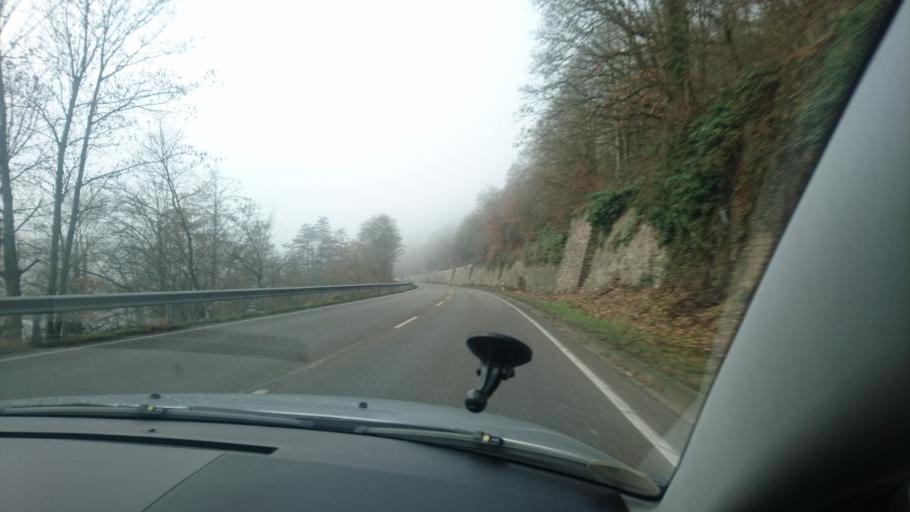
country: DE
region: Rheinland-Pfalz
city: Lahnstein
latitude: 50.3149
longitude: 7.6378
